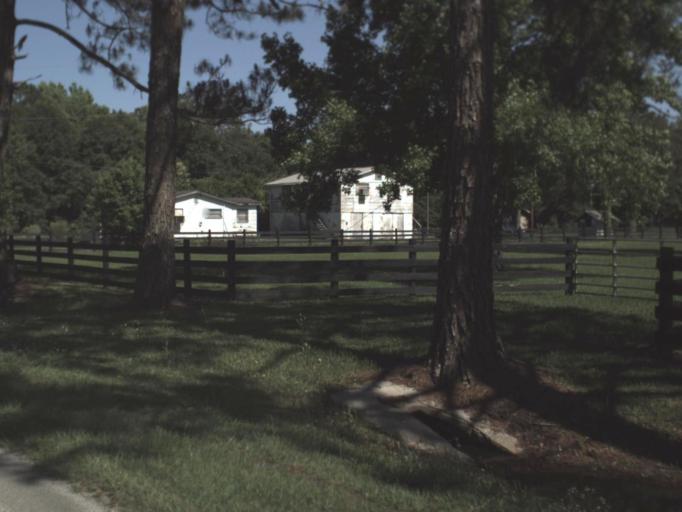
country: US
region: Florida
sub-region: Duval County
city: Baldwin
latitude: 30.3027
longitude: -81.9893
